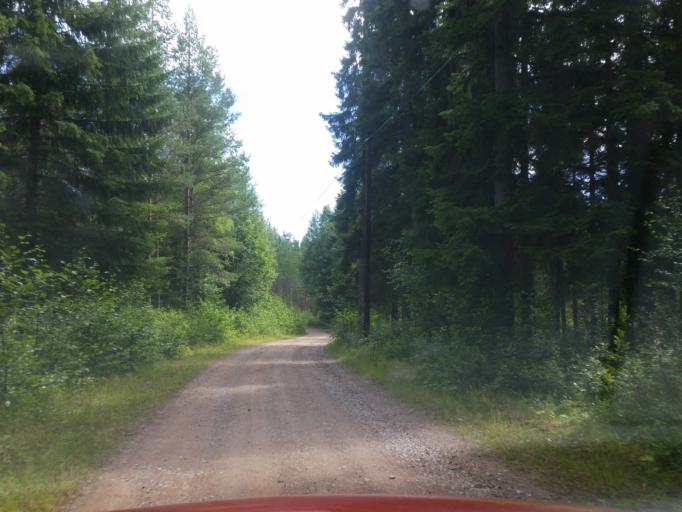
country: SE
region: Dalarna
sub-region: Gagnefs Kommun
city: Gagnef
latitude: 60.6451
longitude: 15.1574
